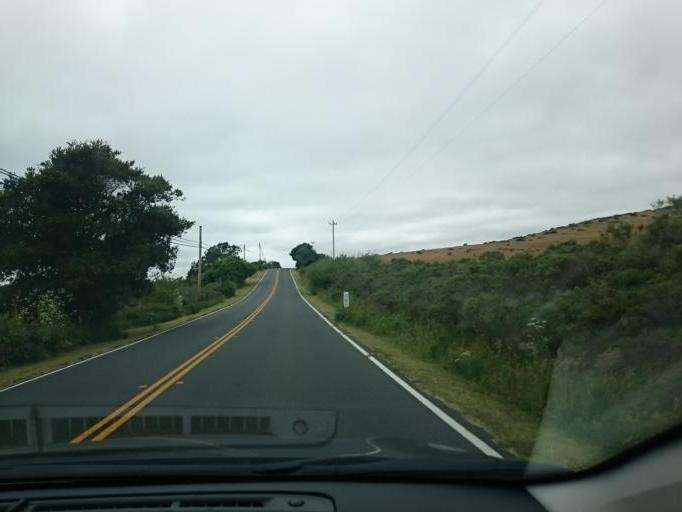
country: US
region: California
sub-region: Marin County
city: Inverness
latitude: 38.1134
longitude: -122.8501
